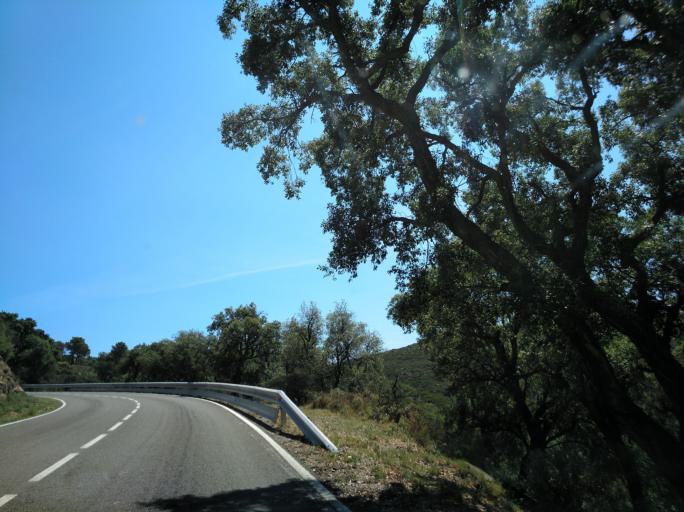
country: ES
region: Catalonia
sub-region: Provincia de Girona
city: Pau
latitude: 42.3290
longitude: 3.1376
